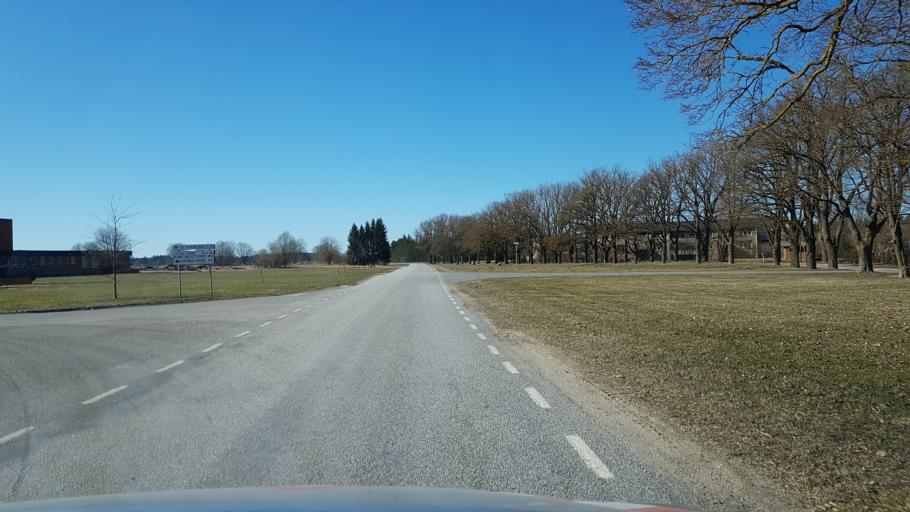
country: EE
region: Laeaene-Virumaa
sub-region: Viru-Nigula vald
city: Kunda
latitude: 59.3936
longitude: 26.5654
